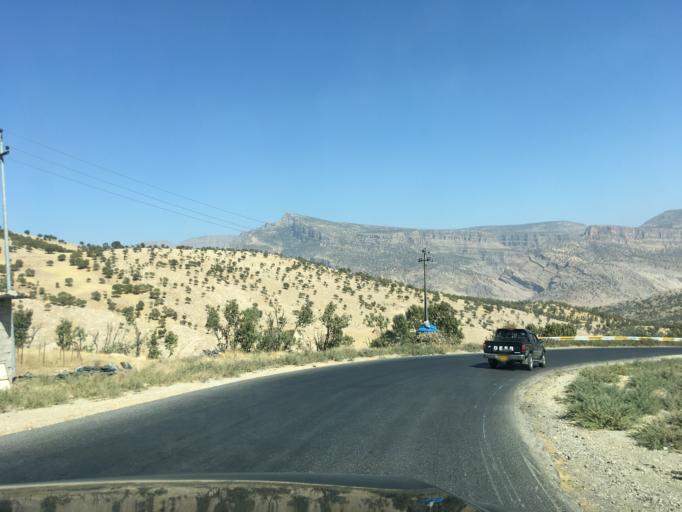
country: IQ
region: Arbil
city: Ruwandiz
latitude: 36.6463
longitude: 44.3428
